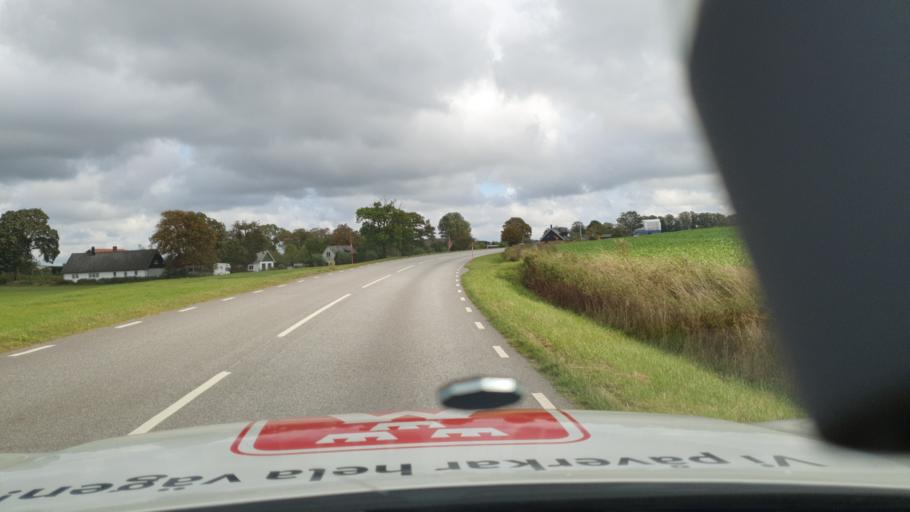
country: SE
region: Skane
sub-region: Malmo
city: Oxie
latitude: 55.4972
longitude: 13.1533
